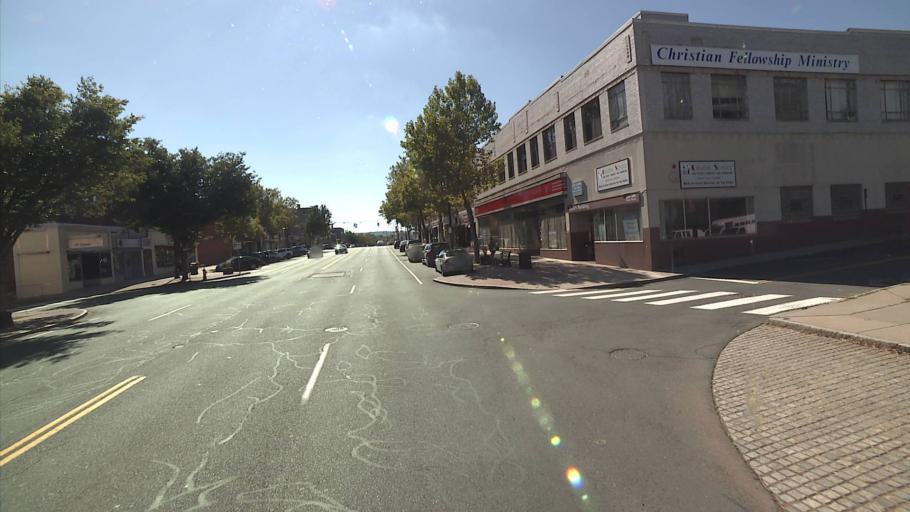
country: US
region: Connecticut
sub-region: Hartford County
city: Manchester
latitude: 41.7716
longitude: -72.5211
